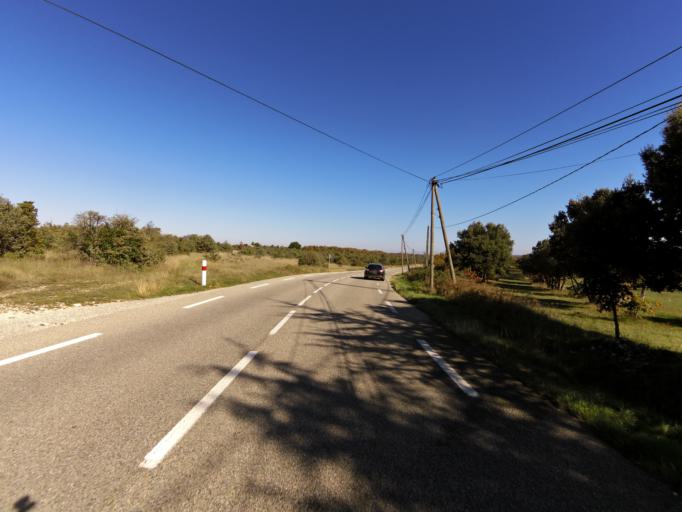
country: FR
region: Languedoc-Roussillon
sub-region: Departement du Gard
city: Saint-Julien-de-Peyrolas
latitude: 44.3899
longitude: 4.5343
